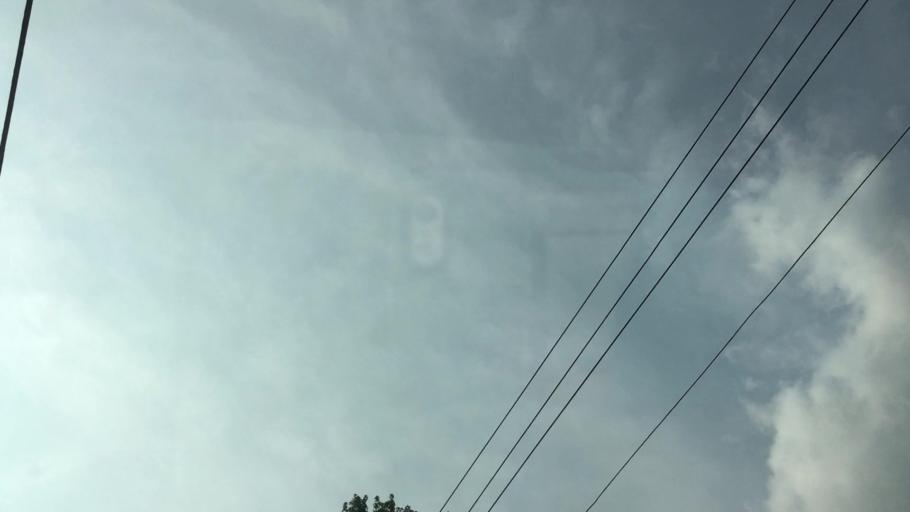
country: US
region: Alabama
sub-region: Bibb County
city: Woodstock
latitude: 33.2235
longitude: -87.1242
